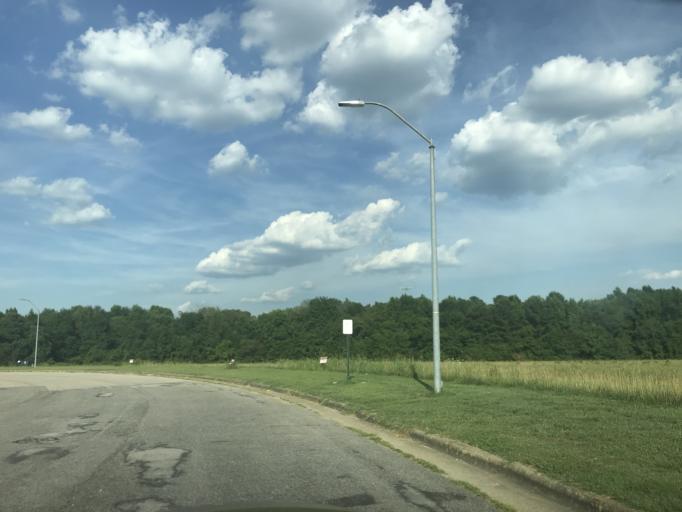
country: US
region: North Carolina
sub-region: Wake County
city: Raleigh
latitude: 35.7556
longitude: -78.6473
